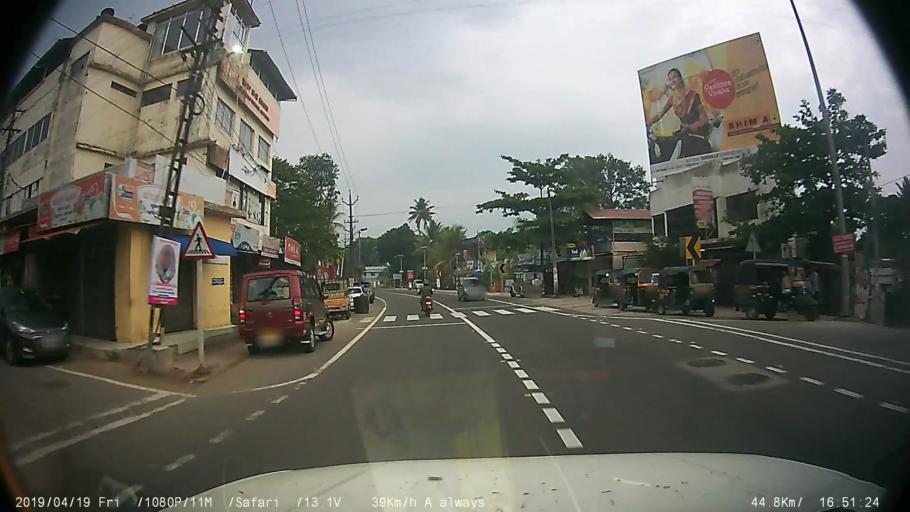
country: IN
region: Kerala
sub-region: Kottayam
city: Changanacheri
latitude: 9.4574
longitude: 76.5335
